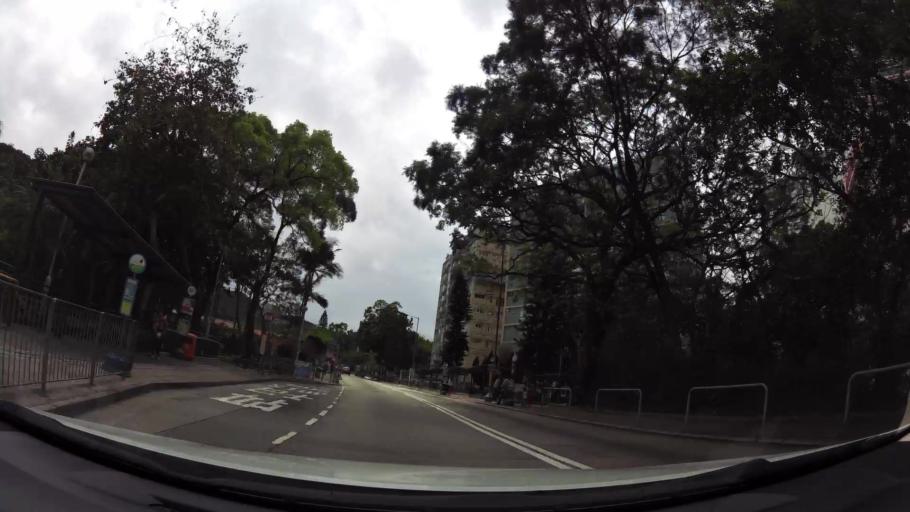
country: HK
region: Wanchai
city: Wan Chai
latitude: 22.2857
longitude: 114.1997
